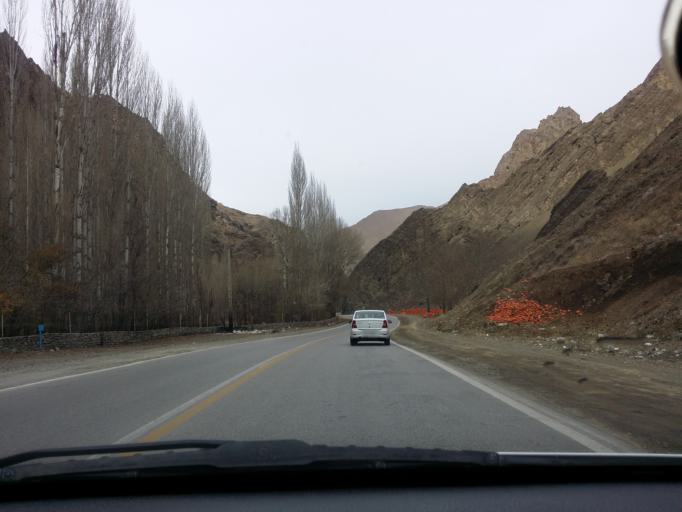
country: IR
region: Tehran
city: Tajrish
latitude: 36.0179
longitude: 51.2706
